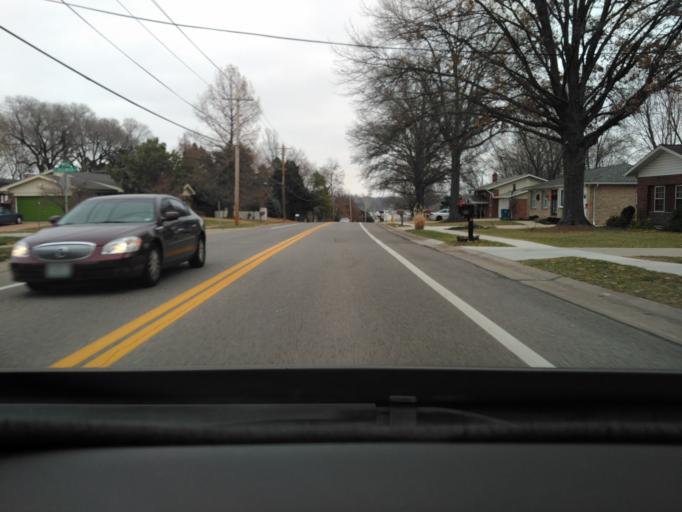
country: US
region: Missouri
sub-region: Saint Louis County
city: Concord
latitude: 38.4962
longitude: -90.3504
